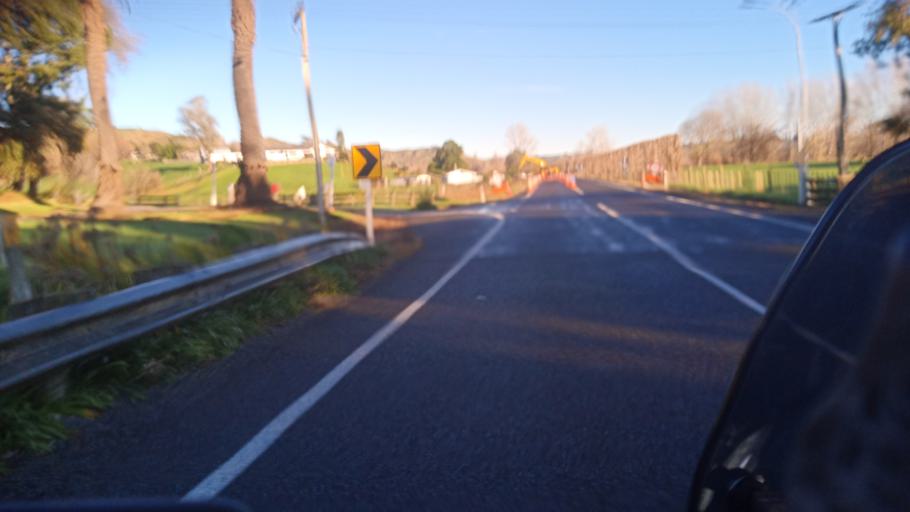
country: NZ
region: Hawke's Bay
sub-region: Wairoa District
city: Wairoa
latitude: -39.0393
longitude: 177.4019
